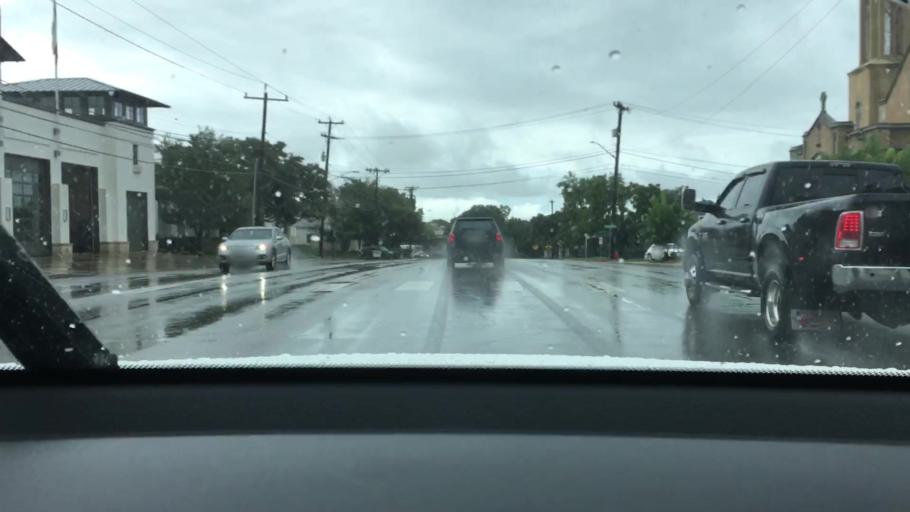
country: US
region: Texas
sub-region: Bexar County
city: Alamo Heights
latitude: 29.4850
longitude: -98.4665
